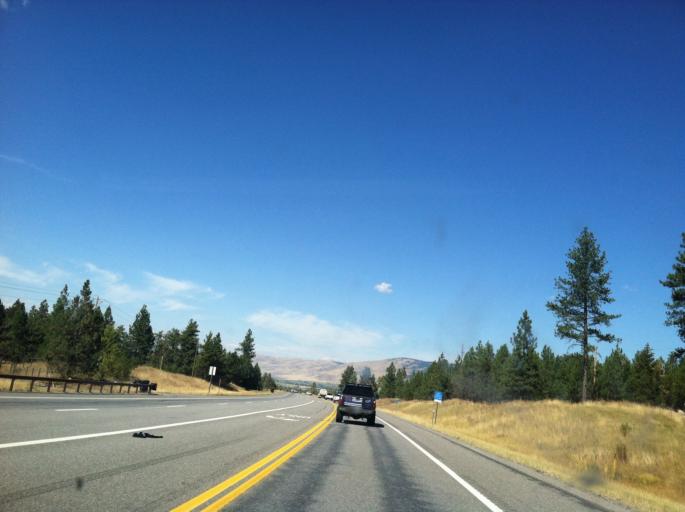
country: US
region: Montana
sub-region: Missoula County
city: Frenchtown
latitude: 47.0936
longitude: -114.0406
